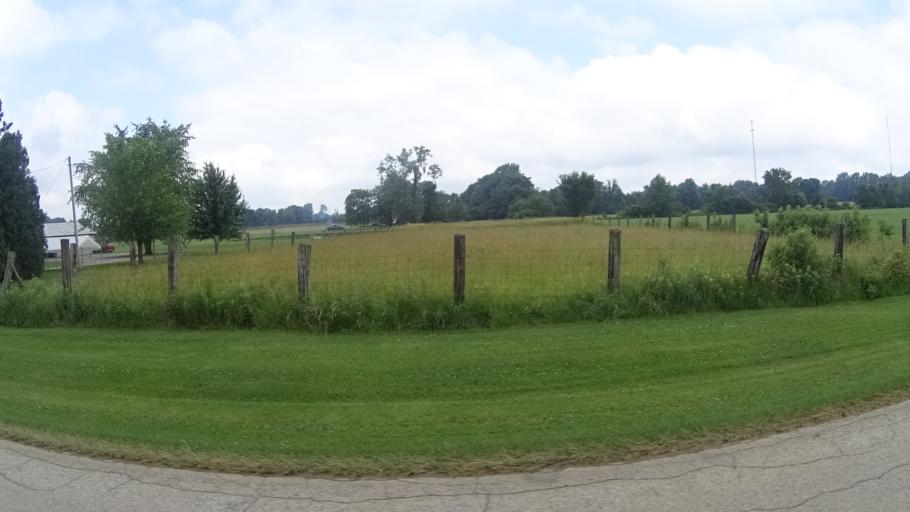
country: US
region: Ohio
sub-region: Huron County
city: Wakeman
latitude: 41.3036
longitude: -82.4430
